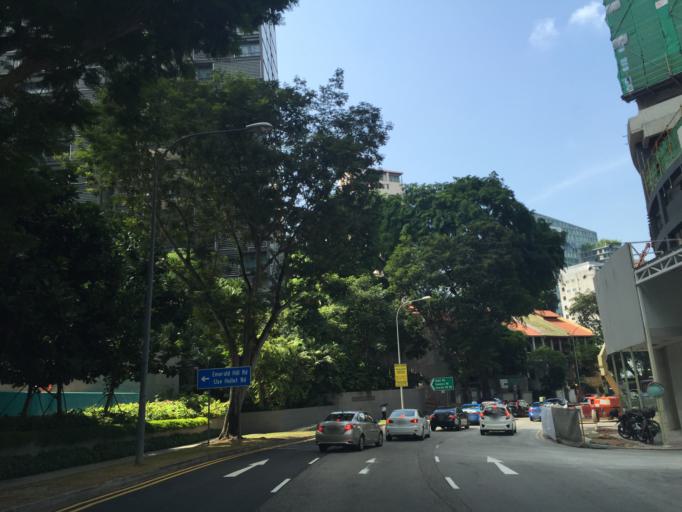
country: SG
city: Singapore
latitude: 1.3042
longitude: 103.8375
